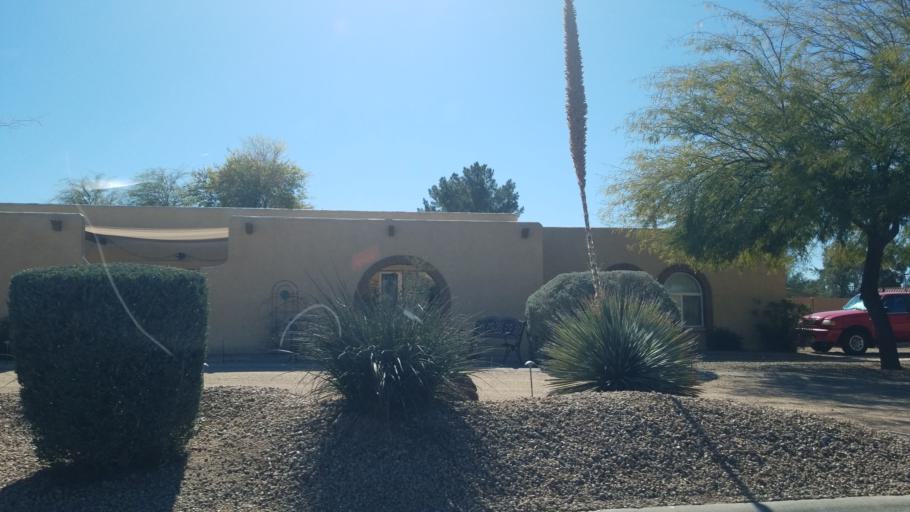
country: US
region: Arizona
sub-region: Maricopa County
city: Paradise Valley
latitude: 33.6149
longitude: -111.9370
